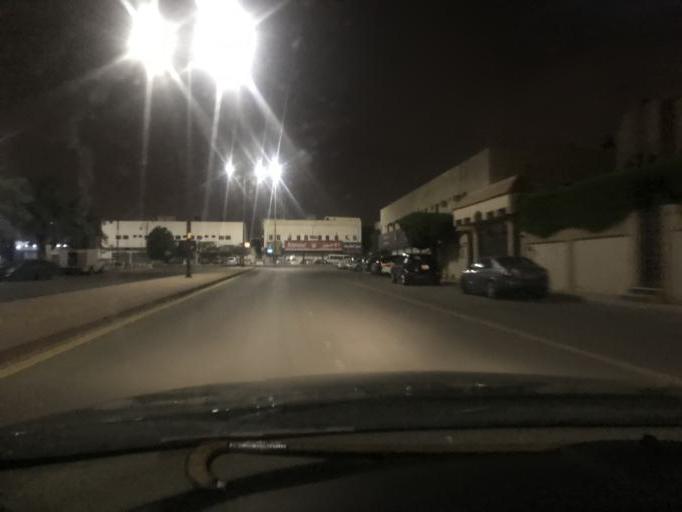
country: SA
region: Ar Riyad
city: Riyadh
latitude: 24.7329
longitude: 46.7762
